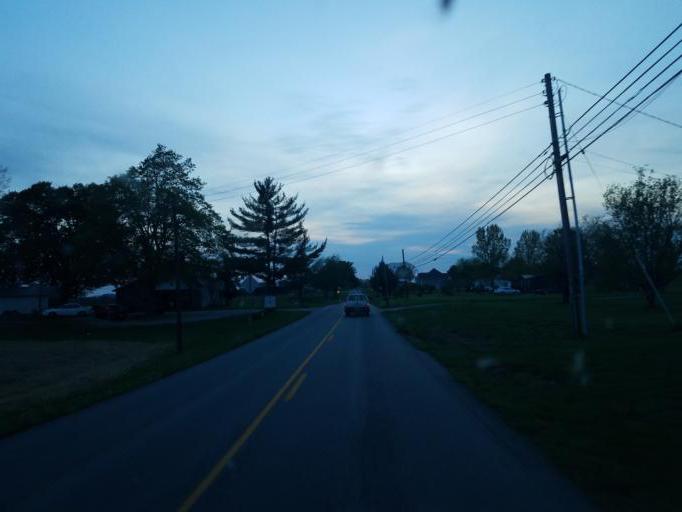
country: US
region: Kentucky
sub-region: Hart County
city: Munfordville
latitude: 37.2730
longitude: -85.8349
